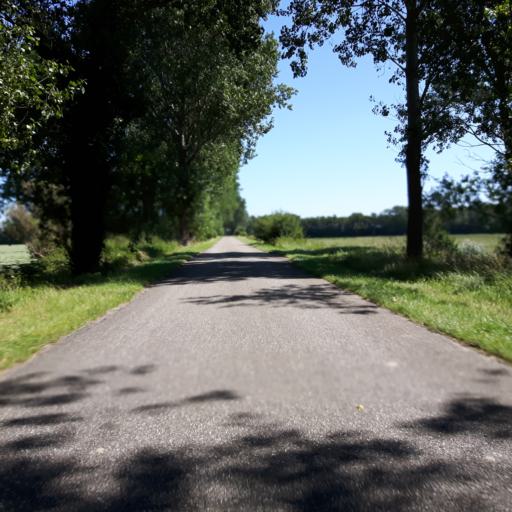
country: NL
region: Zeeland
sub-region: Gemeente Goes
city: Goes
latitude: 51.5629
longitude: 3.8315
